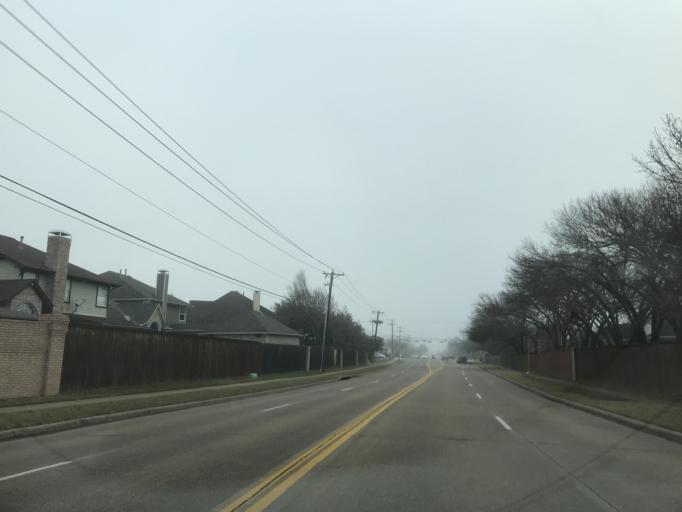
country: US
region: Texas
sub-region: Tarrant County
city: Arlington
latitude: 32.7746
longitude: -97.0757
